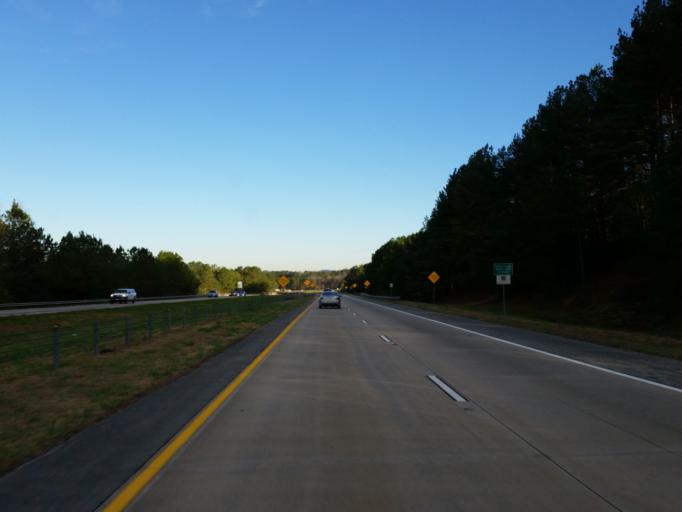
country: US
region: Georgia
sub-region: Pickens County
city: Nelson
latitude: 34.3743
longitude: -84.3923
